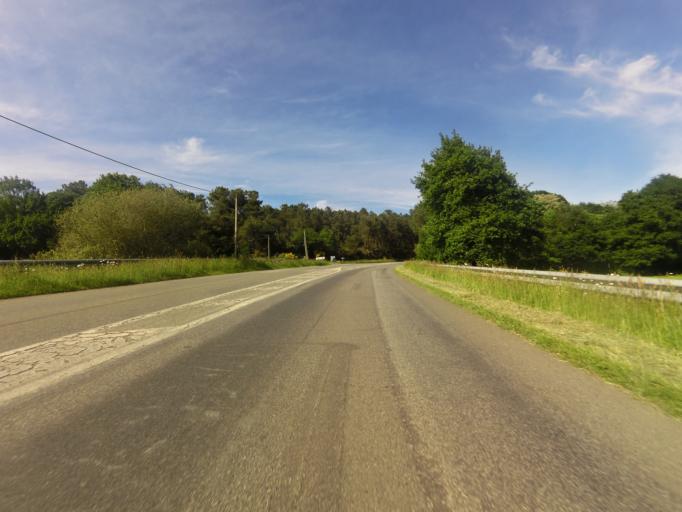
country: FR
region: Brittany
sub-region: Departement du Morbihan
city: Pluherlin
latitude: 47.7045
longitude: -2.3609
